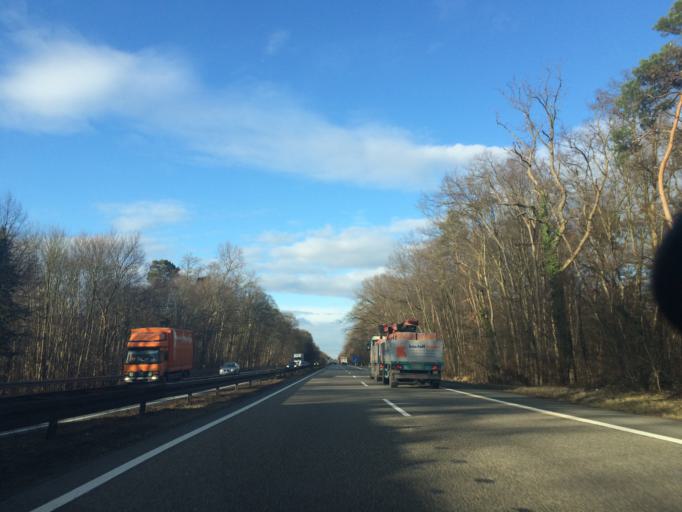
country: DE
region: Hesse
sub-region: Regierungsbezirk Darmstadt
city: Einhausen
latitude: 49.6897
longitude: 8.5516
